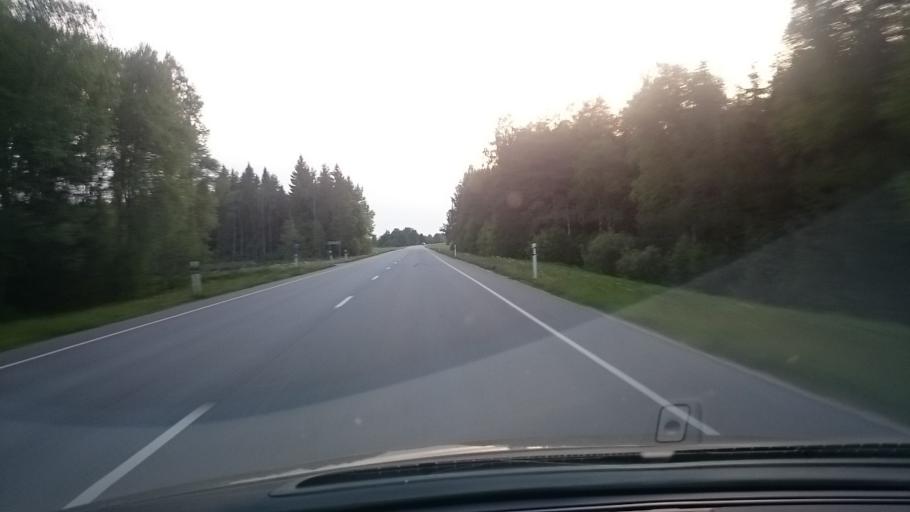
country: EE
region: Jaervamaa
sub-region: Tueri vald
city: Sarevere
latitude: 58.7653
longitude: 25.5371
